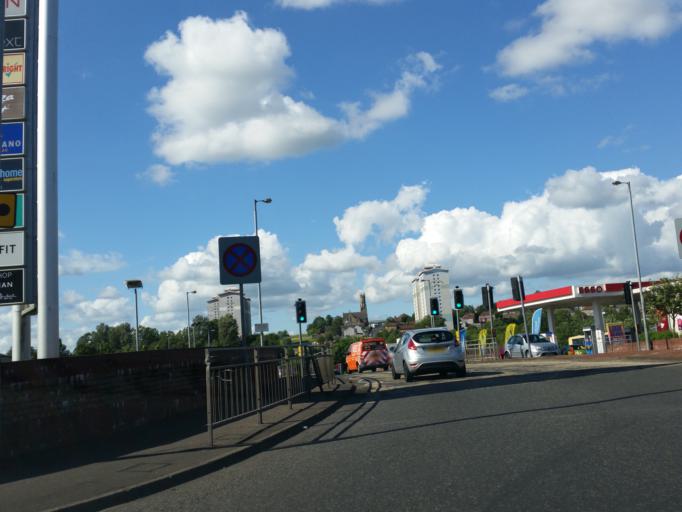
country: GB
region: Scotland
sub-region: North Lanarkshire
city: Coatbridge
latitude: 55.8563
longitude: -4.0203
